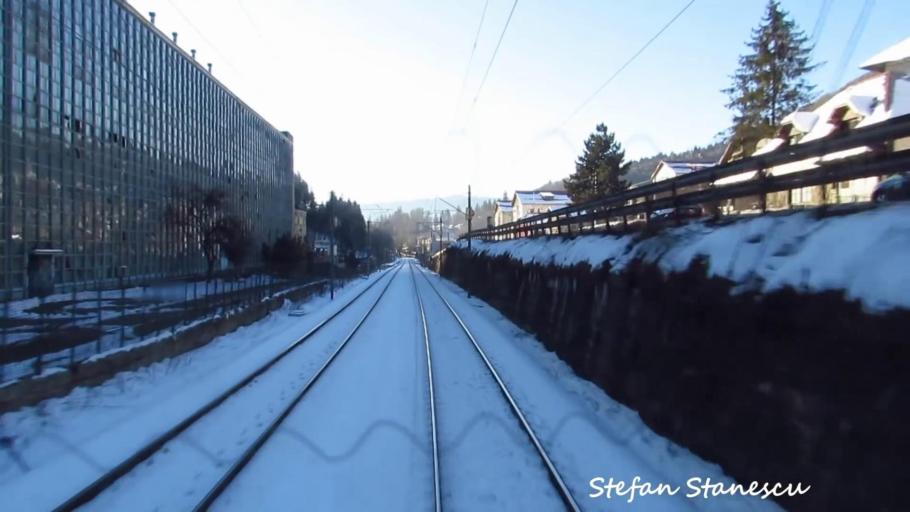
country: RO
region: Prahova
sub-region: Oras Sinaia
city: Sinaia
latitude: 45.3416
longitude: 25.5513
